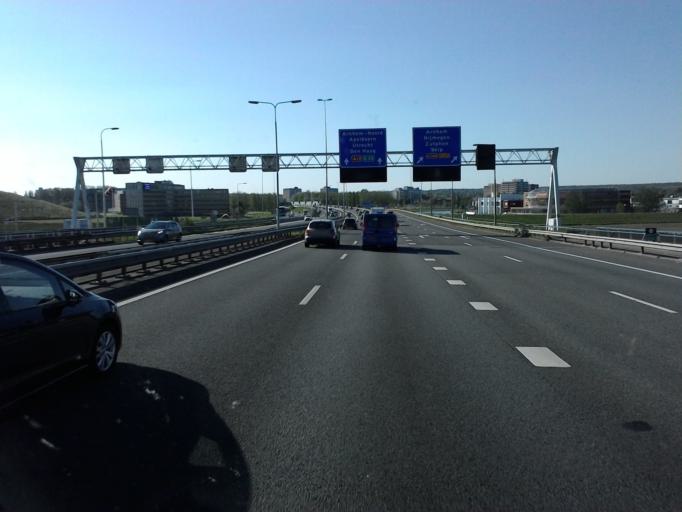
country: NL
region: Gelderland
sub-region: Gemeente Rheden
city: Velp
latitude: 51.9769
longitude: 5.9870
